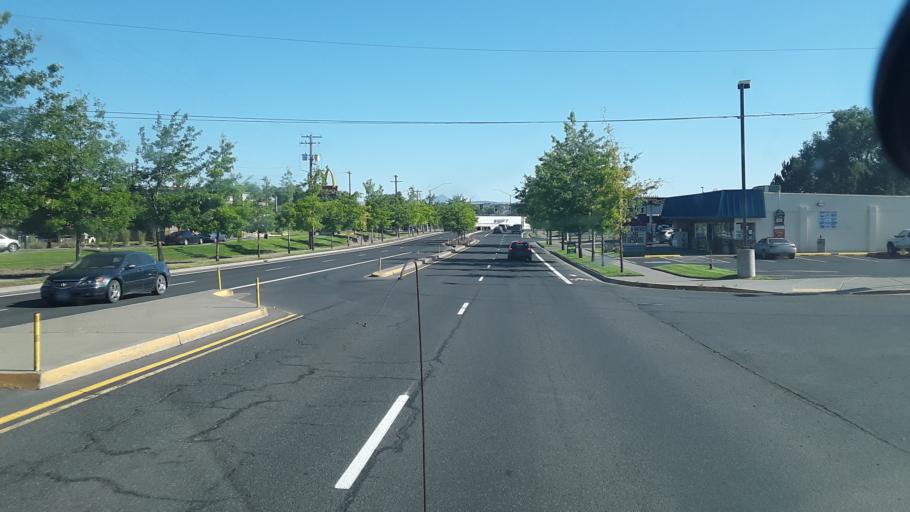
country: US
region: Oregon
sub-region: Jefferson County
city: Madras
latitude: 44.6408
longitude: -121.1297
